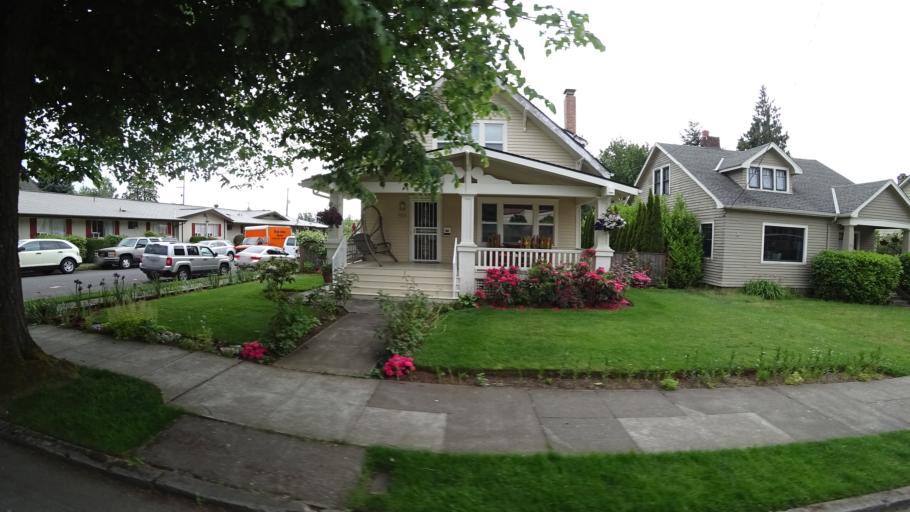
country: US
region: Oregon
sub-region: Multnomah County
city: Lents
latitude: 45.5173
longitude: -122.6126
